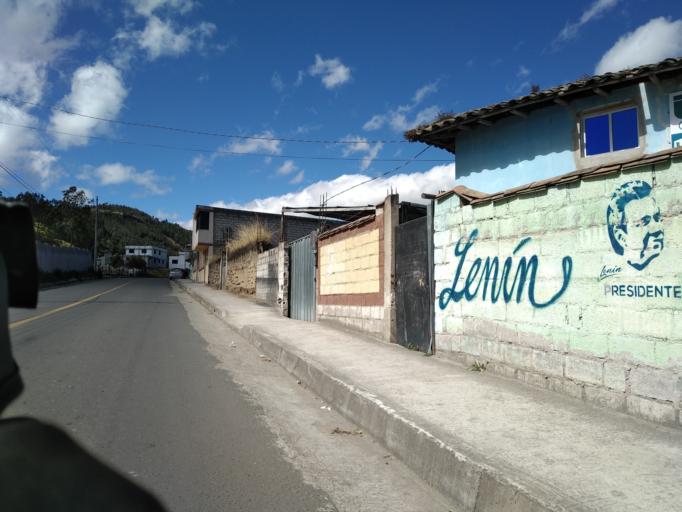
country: EC
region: Imbabura
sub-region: Canton Otavalo
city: Otavalo
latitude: 0.1769
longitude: -78.2049
